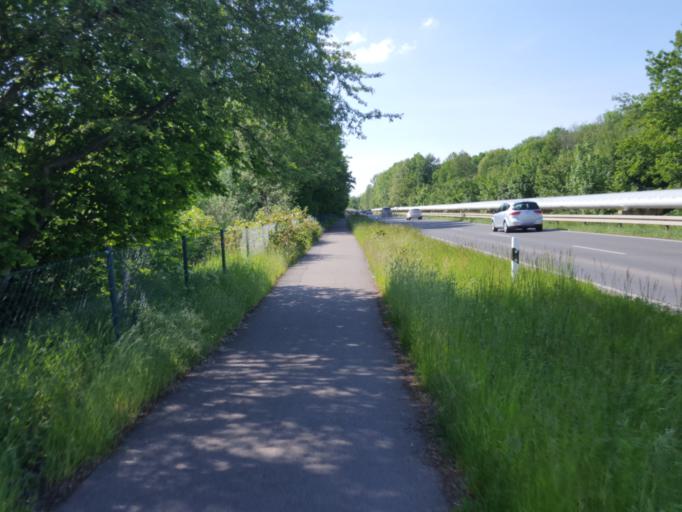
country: DE
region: Saxony
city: Markkleeberg
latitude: 51.2946
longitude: 12.3510
